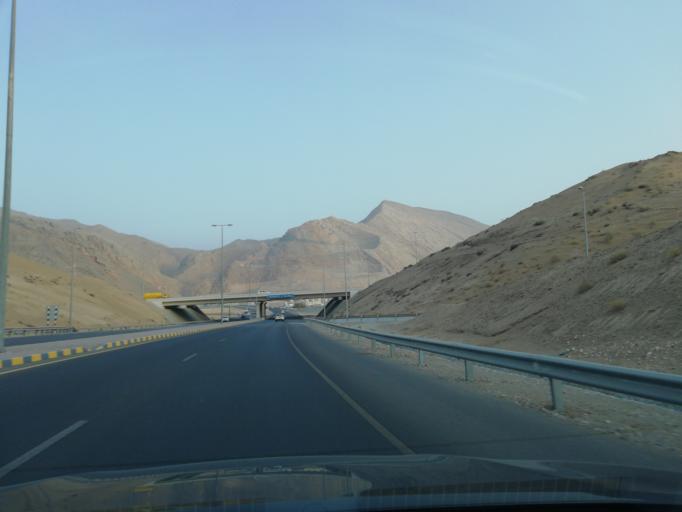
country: OM
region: Muhafazat Masqat
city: Bawshar
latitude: 23.5738
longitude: 58.4245
